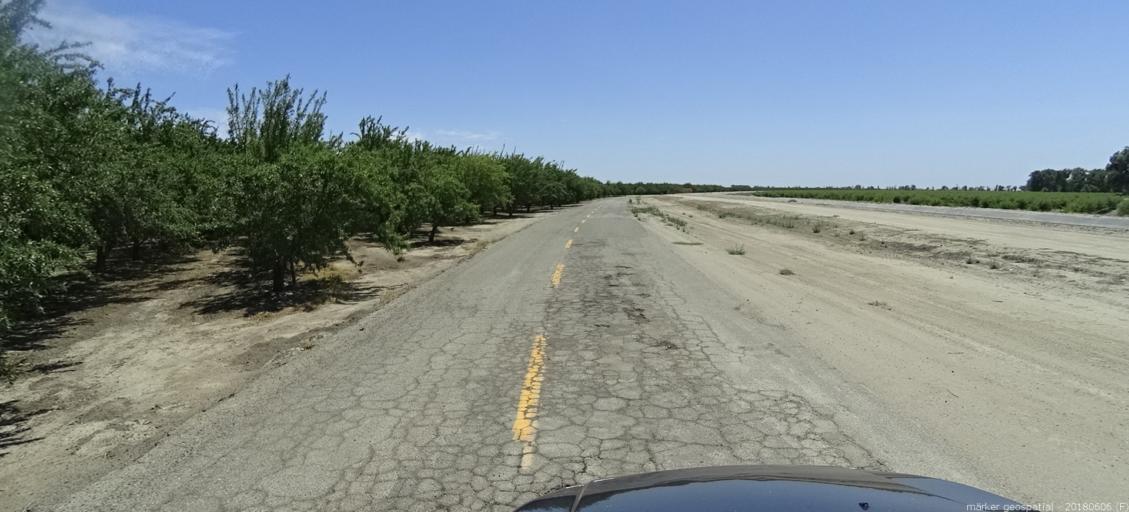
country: US
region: California
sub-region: Fresno County
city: Firebaugh
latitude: 36.8406
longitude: -120.4091
